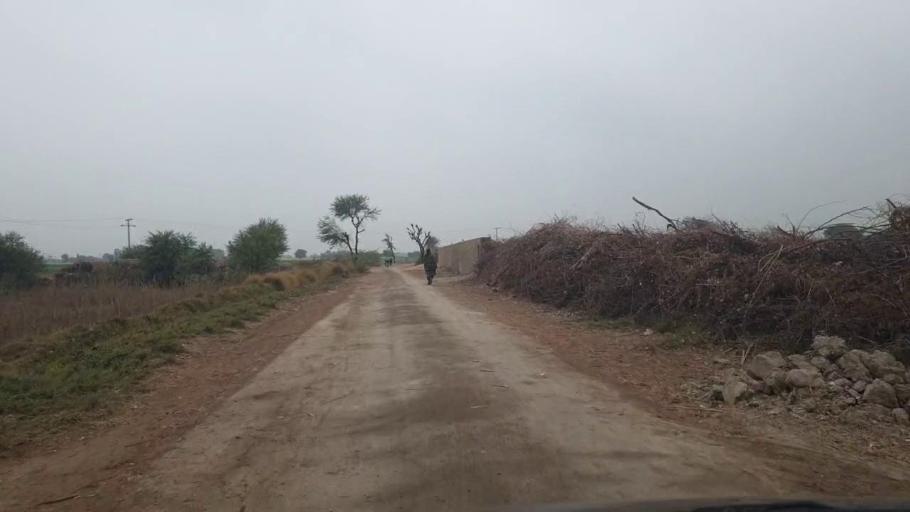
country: PK
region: Sindh
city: Tando Adam
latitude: 25.8421
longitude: 68.7233
